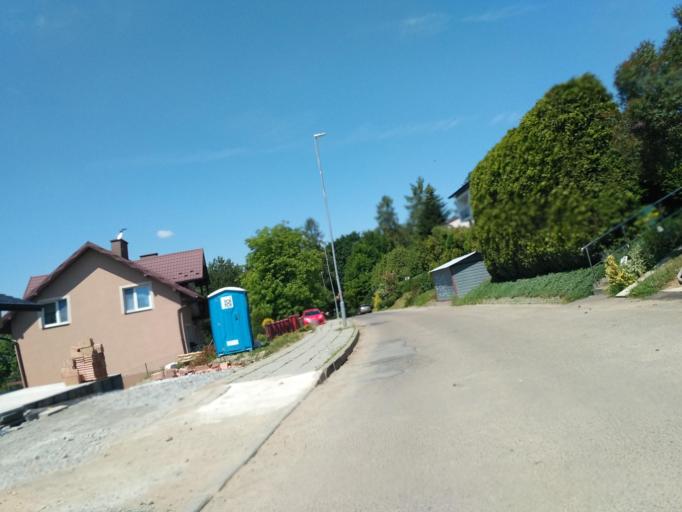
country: PL
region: Subcarpathian Voivodeship
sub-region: Krosno
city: Krosno
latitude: 49.6999
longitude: 21.7683
